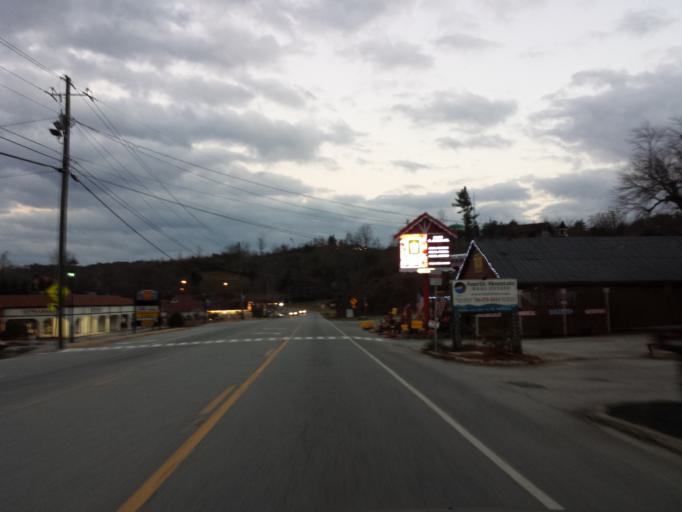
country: US
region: Georgia
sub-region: White County
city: Cleveland
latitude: 34.6984
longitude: -83.7212
